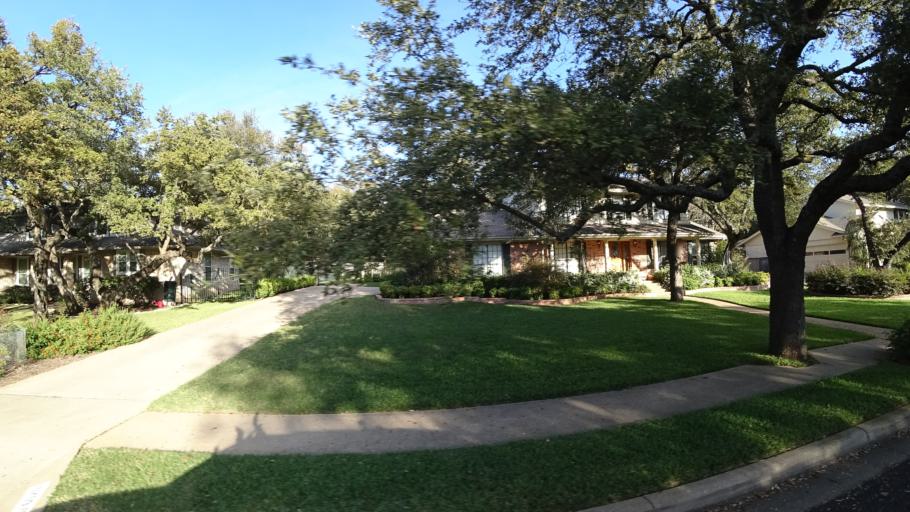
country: US
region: Texas
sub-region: Williamson County
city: Anderson Mill
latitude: 30.4350
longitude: -97.8074
